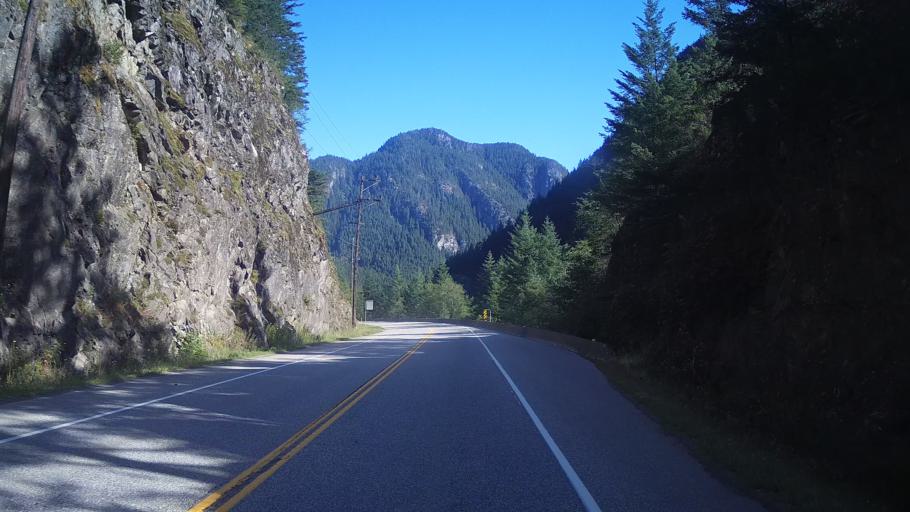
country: CA
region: British Columbia
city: Hope
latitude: 49.5930
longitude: -121.4101
